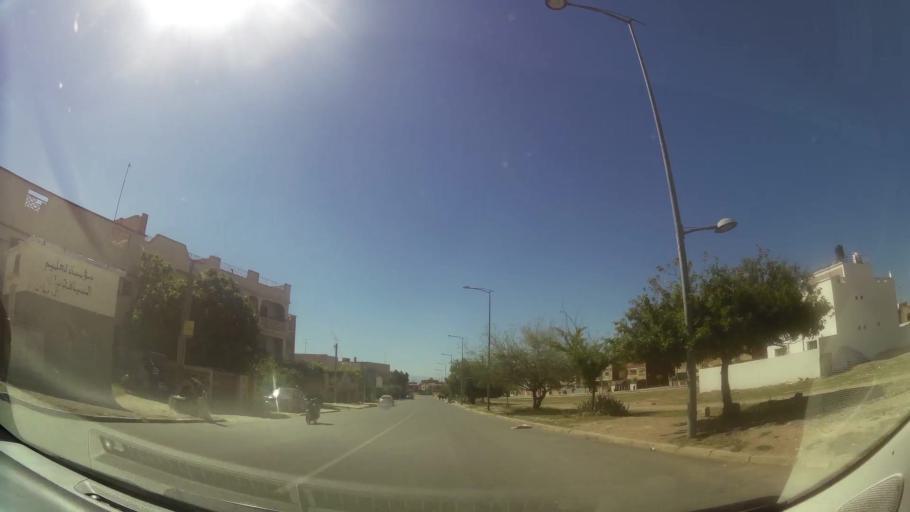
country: MA
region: Oriental
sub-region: Oujda-Angad
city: Oujda
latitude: 34.6666
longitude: -1.8701
